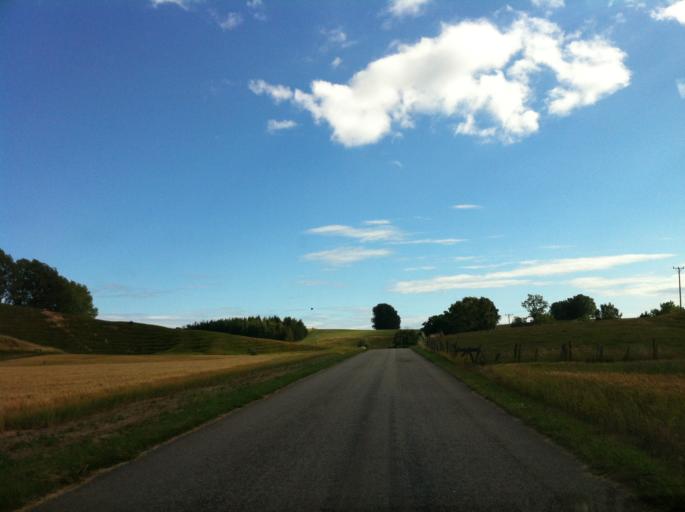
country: SE
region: Skane
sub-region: Ystads Kommun
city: Kopingebro
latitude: 55.3950
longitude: 14.0391
